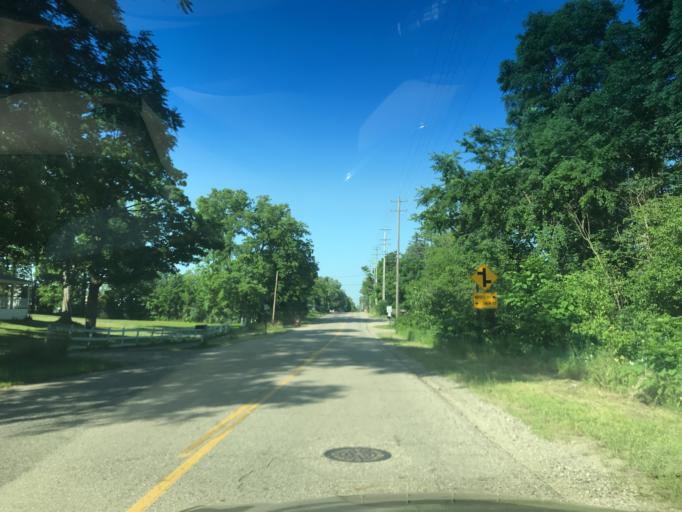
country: US
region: Michigan
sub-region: Eaton County
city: Waverly
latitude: 42.6973
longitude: -84.6252
